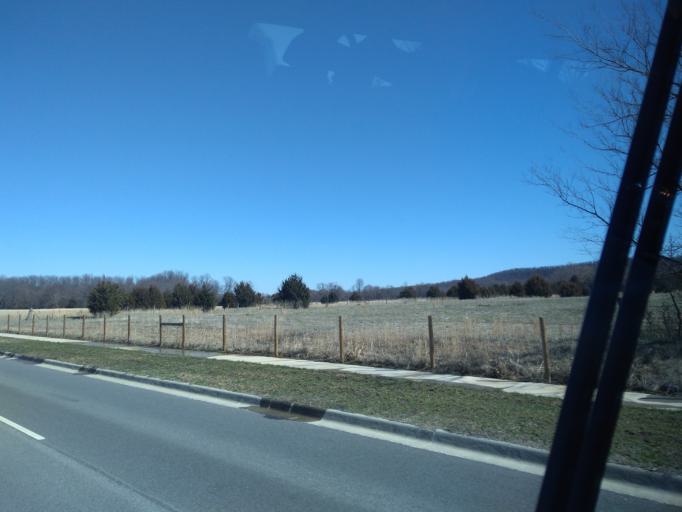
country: US
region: Arkansas
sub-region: Washington County
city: Farmington
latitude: 36.0613
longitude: -94.2202
